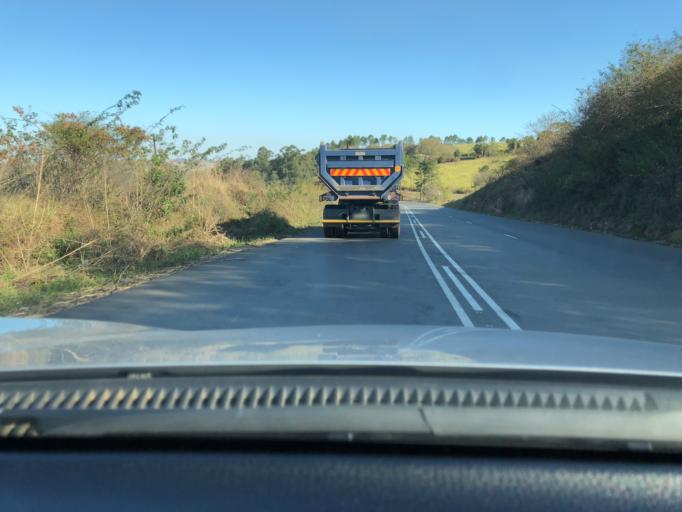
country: ZA
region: KwaZulu-Natal
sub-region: uMgungundlovu District Municipality
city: Camperdown
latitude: -29.7822
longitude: 30.5079
